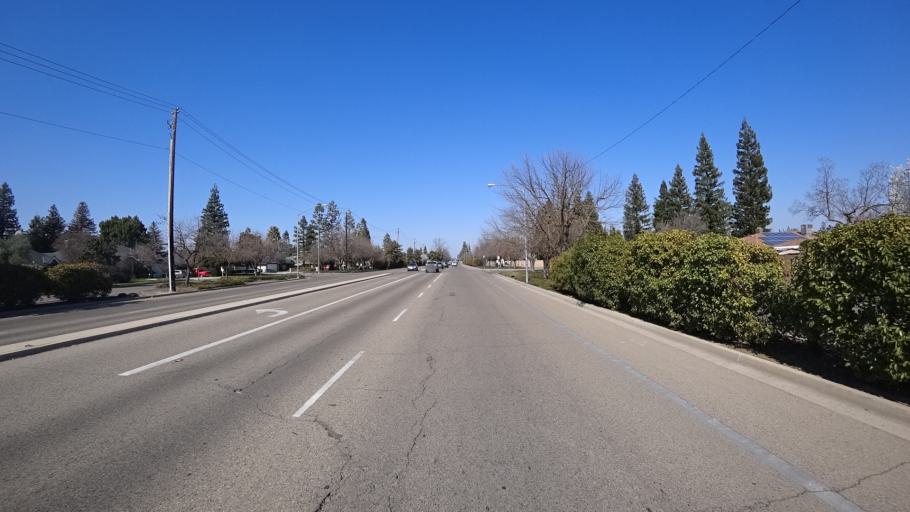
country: US
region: California
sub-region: Fresno County
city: Clovis
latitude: 36.8478
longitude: -119.7567
